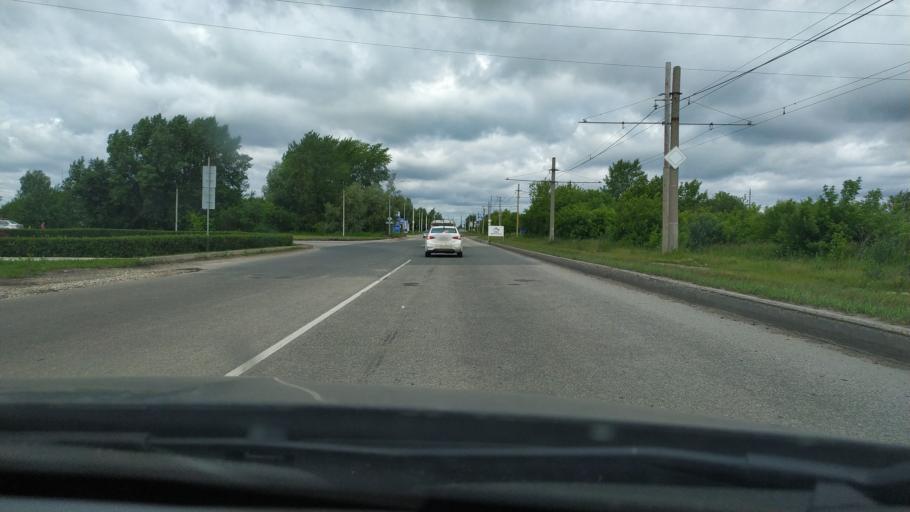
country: RU
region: Perm
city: Kondratovo
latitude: 57.9316
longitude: 56.1268
